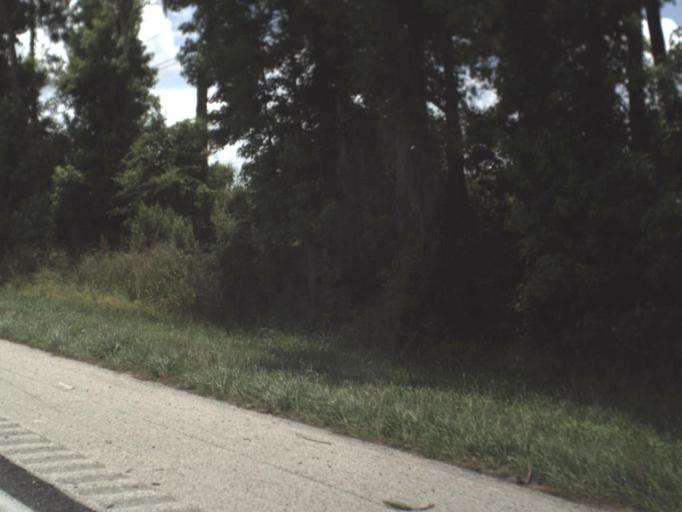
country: US
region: Florida
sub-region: Alachua County
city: Alachua
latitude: 29.7416
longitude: -82.4809
